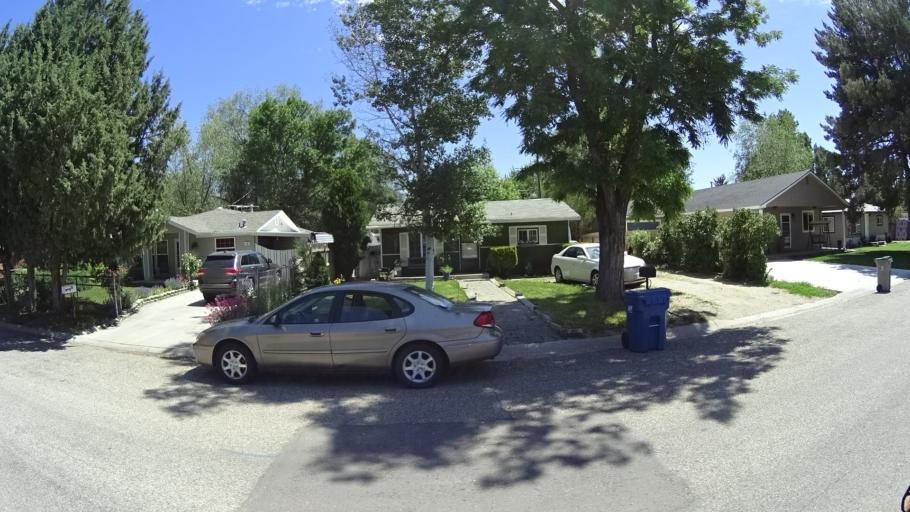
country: US
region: Idaho
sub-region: Ada County
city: Boise
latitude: 43.6036
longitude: -116.2236
